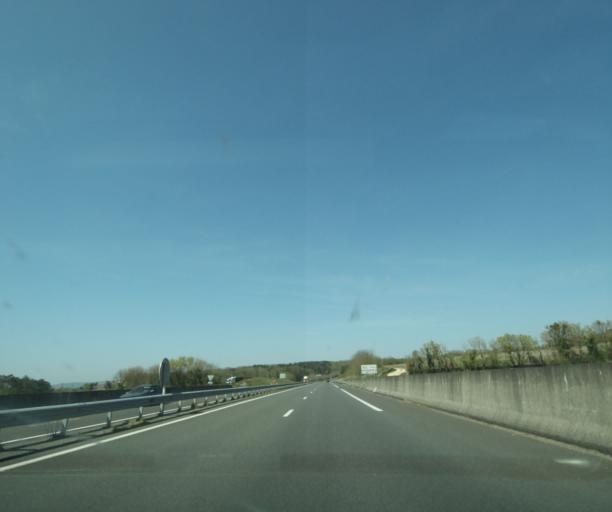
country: FR
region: Bourgogne
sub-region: Departement de la Nievre
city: Pouilly-sur-Loire
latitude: 47.2870
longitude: 2.9630
